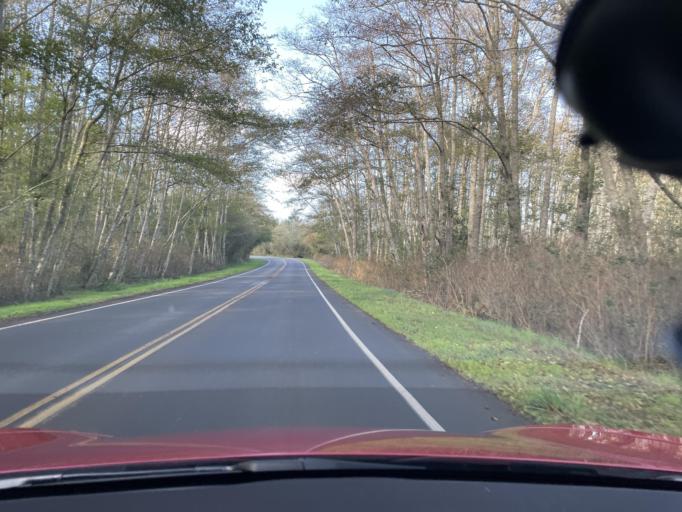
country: US
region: Washington
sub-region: San Juan County
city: Friday Harbor
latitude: 48.4667
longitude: -123.0065
